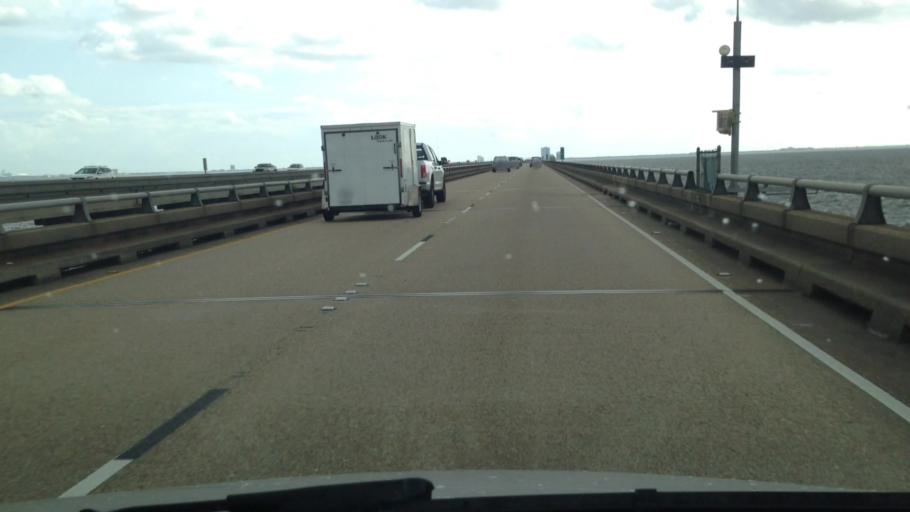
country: US
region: Louisiana
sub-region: Jefferson Parish
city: Metairie
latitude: 30.0975
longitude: -90.1409
